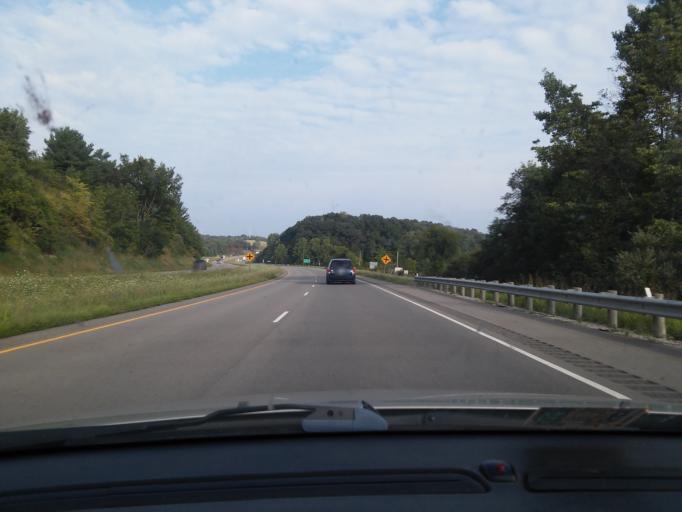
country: US
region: Ohio
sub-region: Jackson County
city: Oak Hill
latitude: 38.9546
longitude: -82.4886
